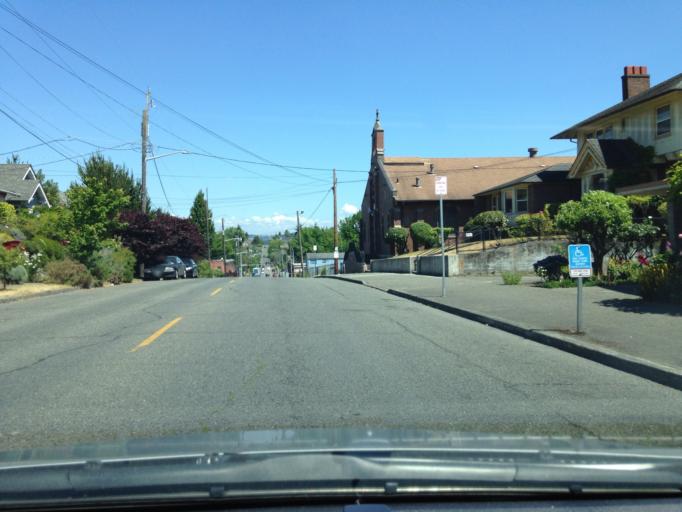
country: US
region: Washington
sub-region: King County
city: Mercer Island
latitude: 47.5512
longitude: -122.2806
